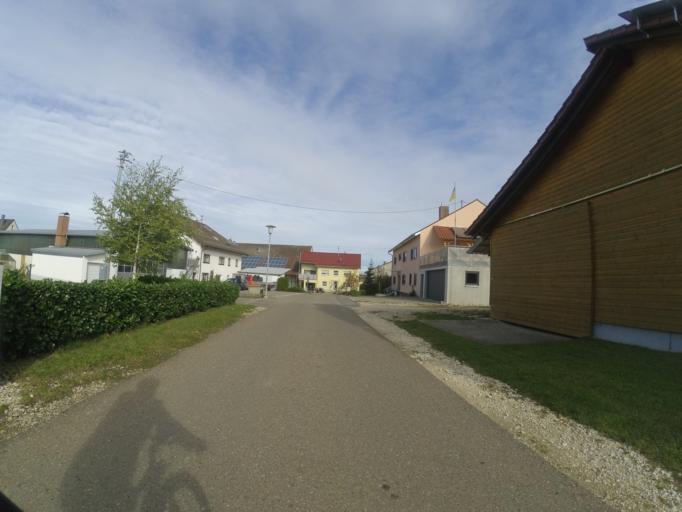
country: DE
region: Baden-Wuerttemberg
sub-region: Tuebingen Region
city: Lonsee
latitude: 48.5652
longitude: 9.9258
